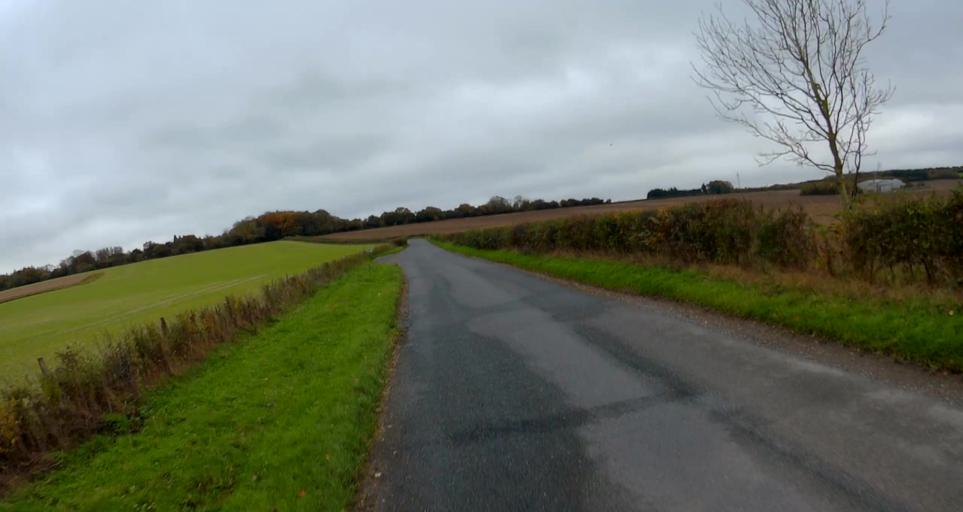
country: GB
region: England
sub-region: Hampshire
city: Basingstoke
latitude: 51.2259
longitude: -1.1264
